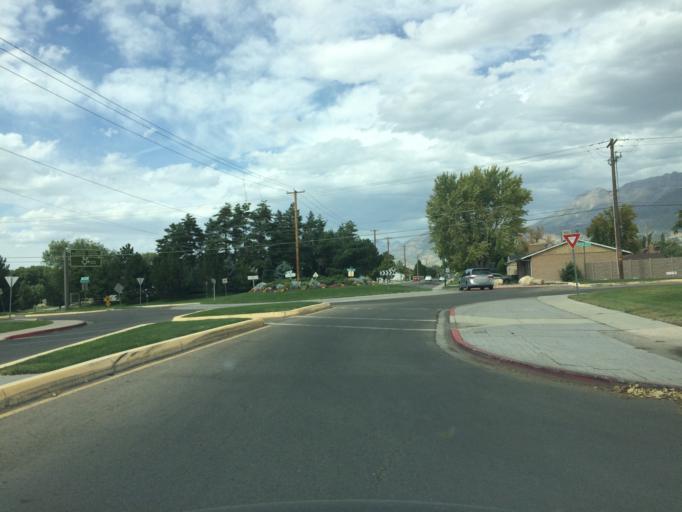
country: US
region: Utah
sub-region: Utah County
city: Orem
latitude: 40.2749
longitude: -111.7046
